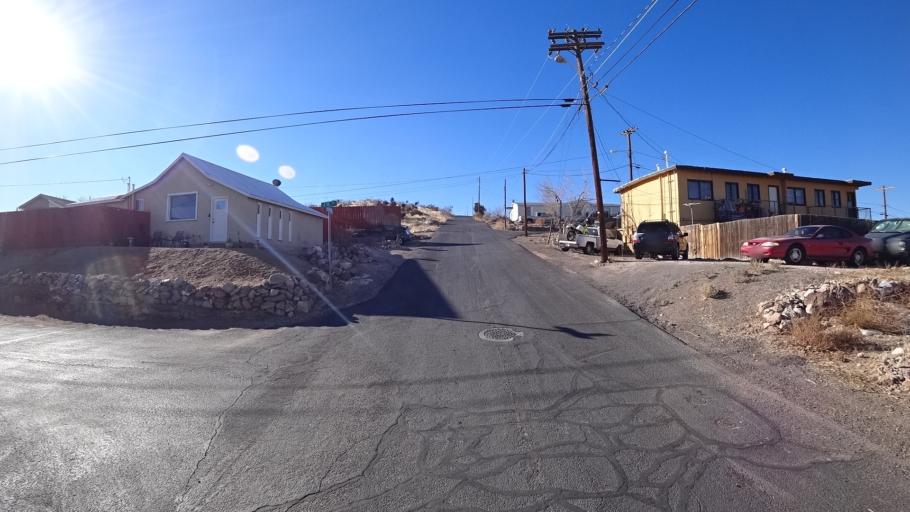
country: US
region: Arizona
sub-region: Mohave County
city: Kingman
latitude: 35.1847
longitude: -114.0520
